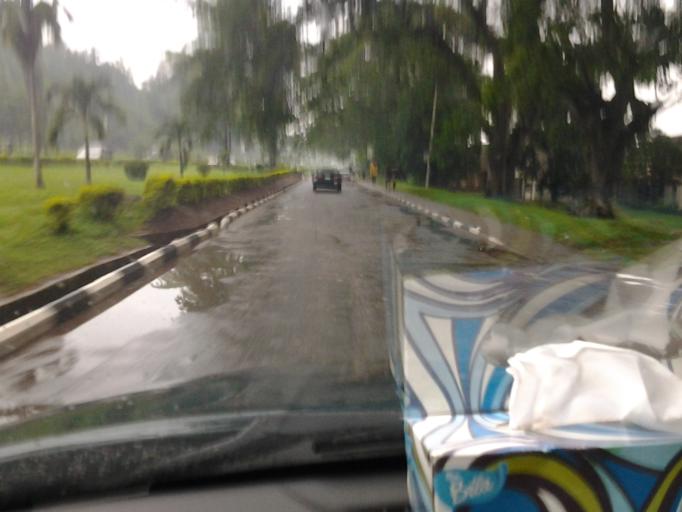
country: NG
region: Oyo
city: Ibadan
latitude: 7.4440
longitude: 3.9014
